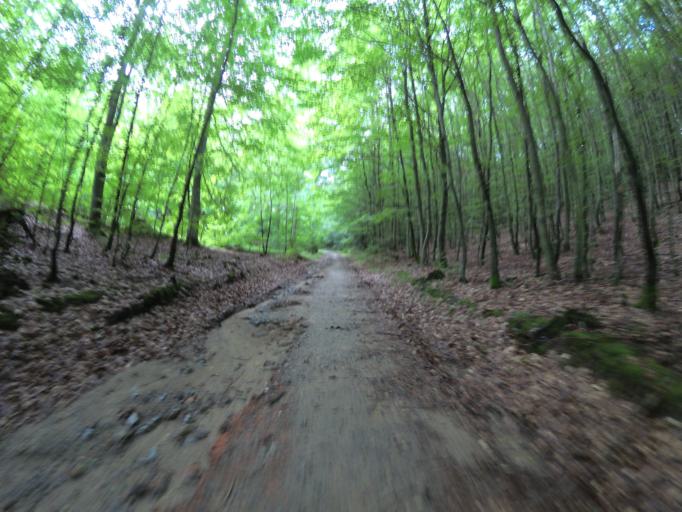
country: PL
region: Pomeranian Voivodeship
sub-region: Gdynia
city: Wielki Kack
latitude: 54.5102
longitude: 18.4441
